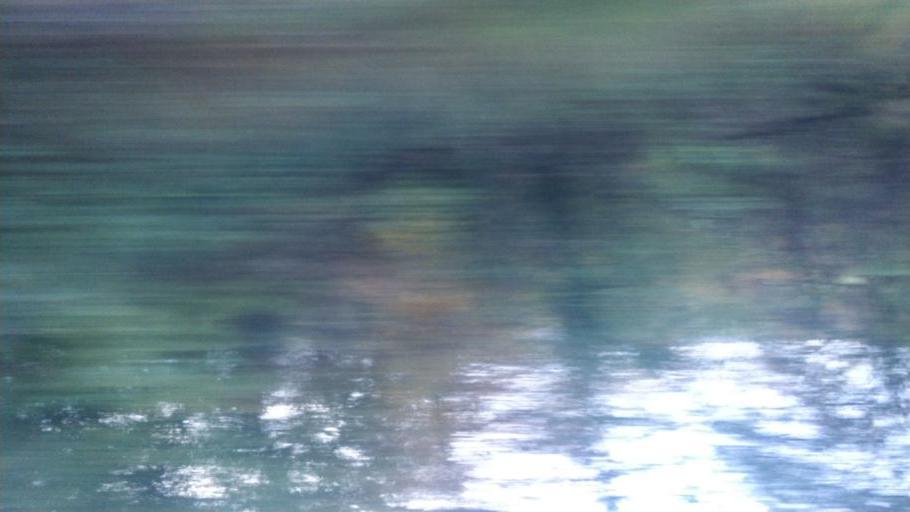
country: GB
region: England
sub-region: Lancashire
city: Appley Bridge
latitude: 53.5843
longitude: -2.7433
